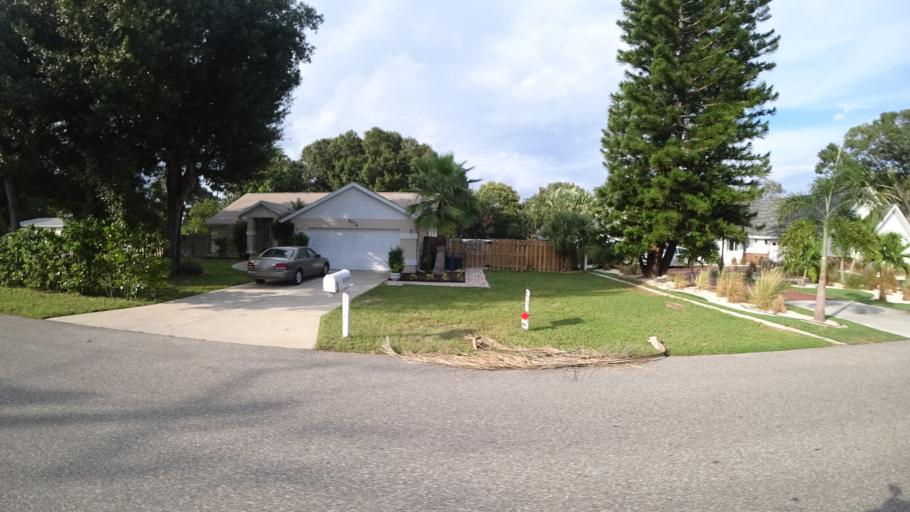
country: US
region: Florida
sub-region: Manatee County
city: West Bradenton
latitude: 27.4838
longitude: -82.6119
